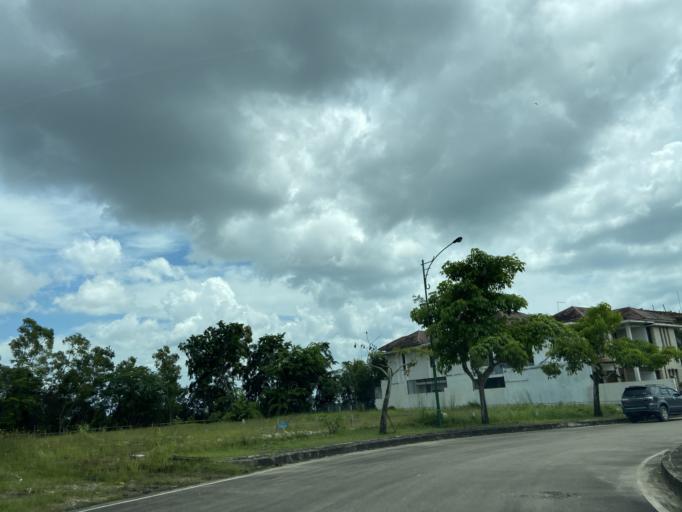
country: SG
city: Singapore
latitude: 1.1266
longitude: 104.0008
